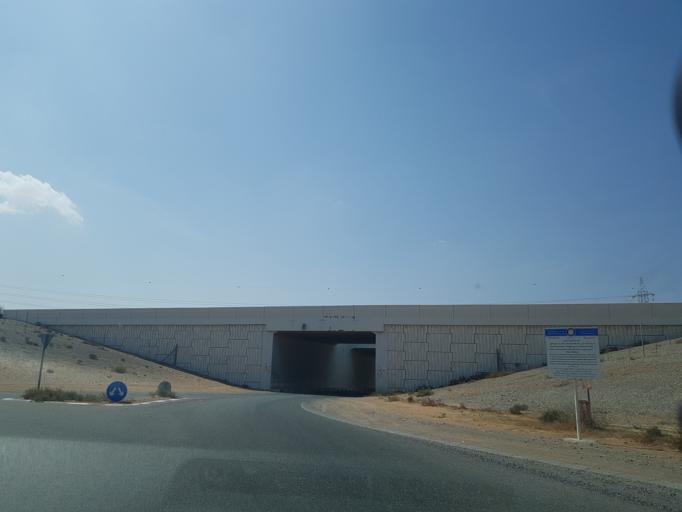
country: AE
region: Ra's al Khaymah
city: Ras al-Khaimah
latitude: 25.6998
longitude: 55.8744
